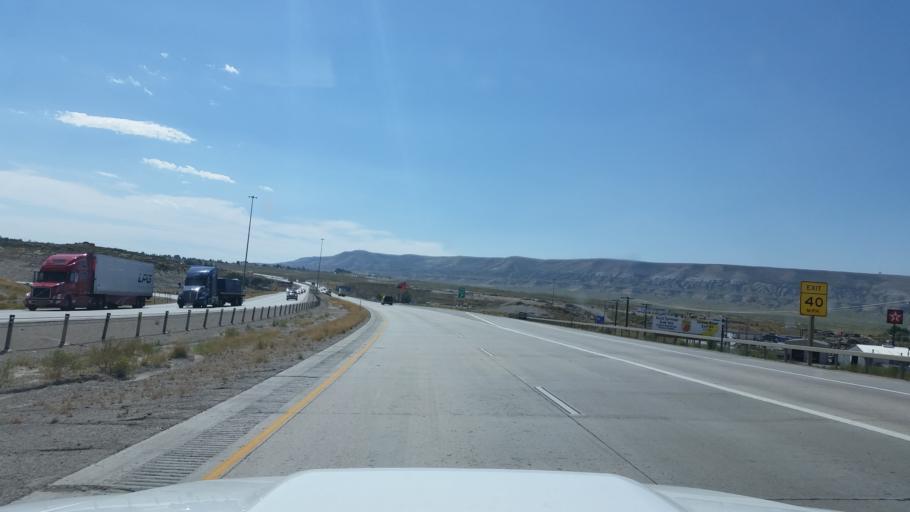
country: US
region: Wyoming
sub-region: Sweetwater County
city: Rock Springs
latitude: 41.6100
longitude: -109.2235
